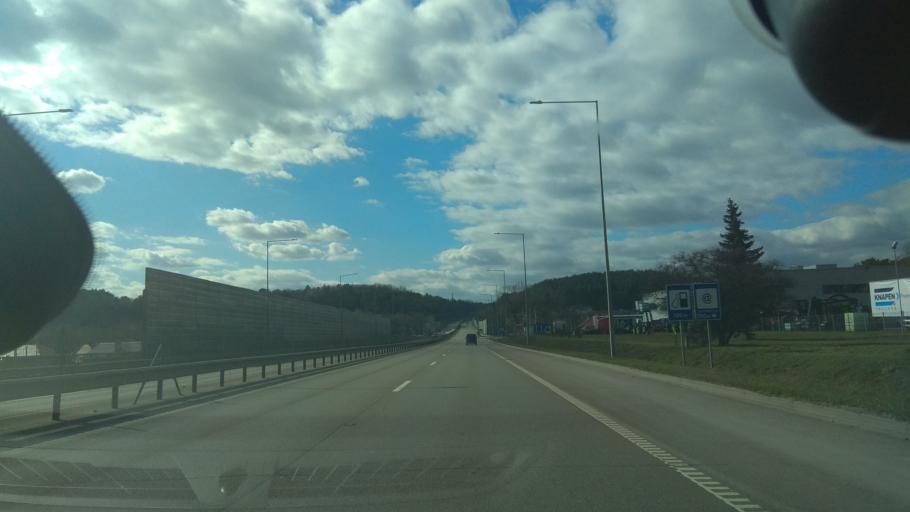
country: LT
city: Grigiskes
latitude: 54.6769
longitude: 25.0815
